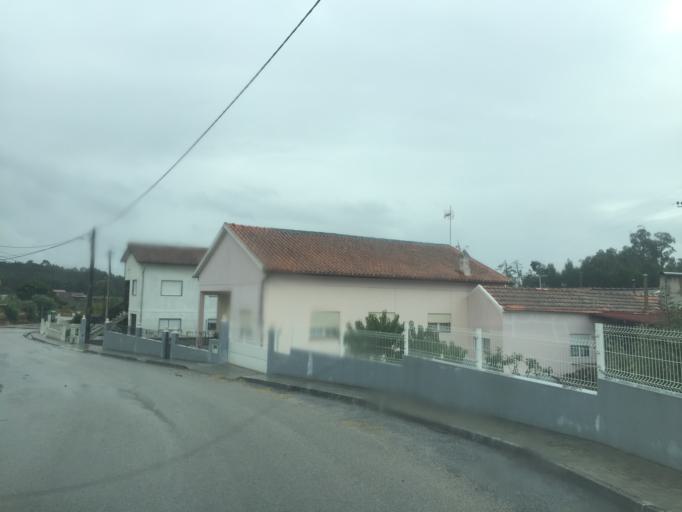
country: PT
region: Coimbra
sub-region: Figueira da Foz
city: Lavos
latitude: 40.0655
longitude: -8.7778
